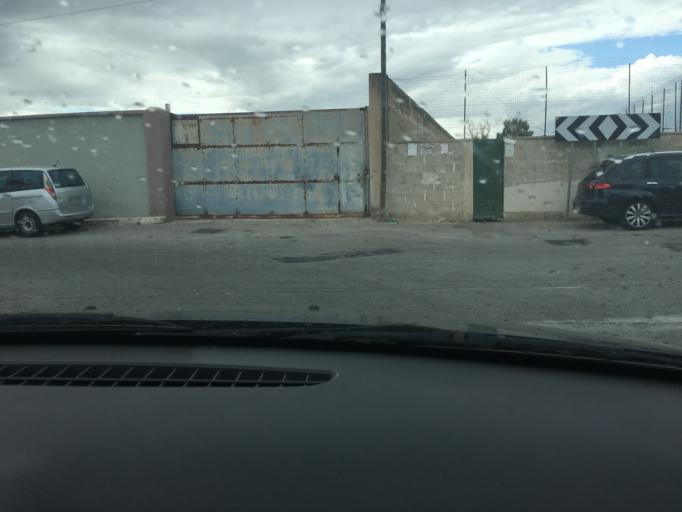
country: IT
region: Apulia
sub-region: Provincia di Bari
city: San Paolo
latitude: 41.1347
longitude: 16.8235
